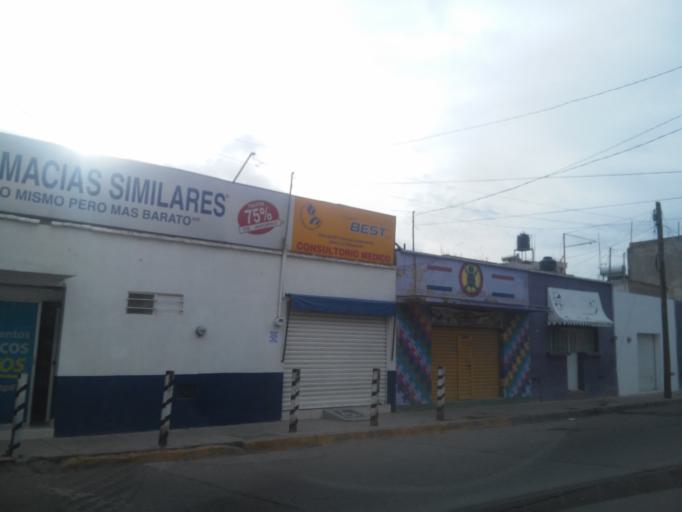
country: MX
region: Durango
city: Victoria de Durango
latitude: 24.0117
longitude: -104.6750
